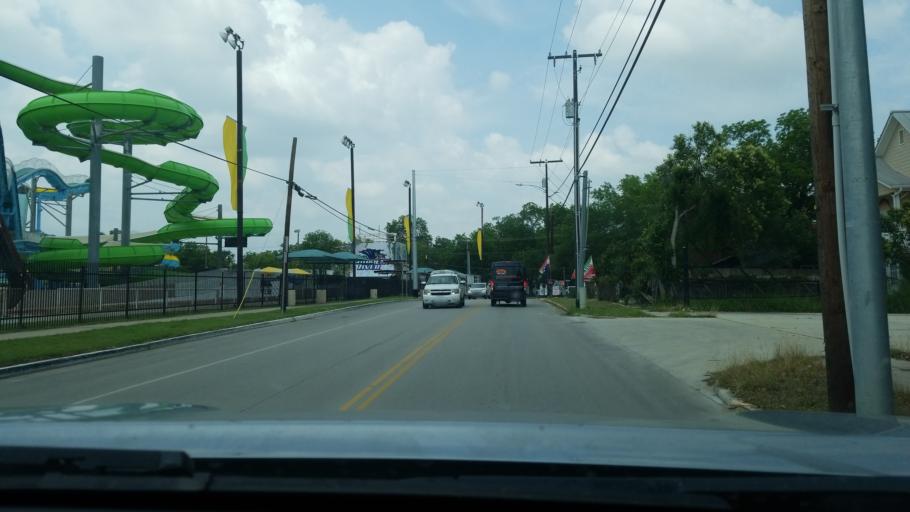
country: US
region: Texas
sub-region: Comal County
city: New Braunfels
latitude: 29.7038
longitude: -98.1172
